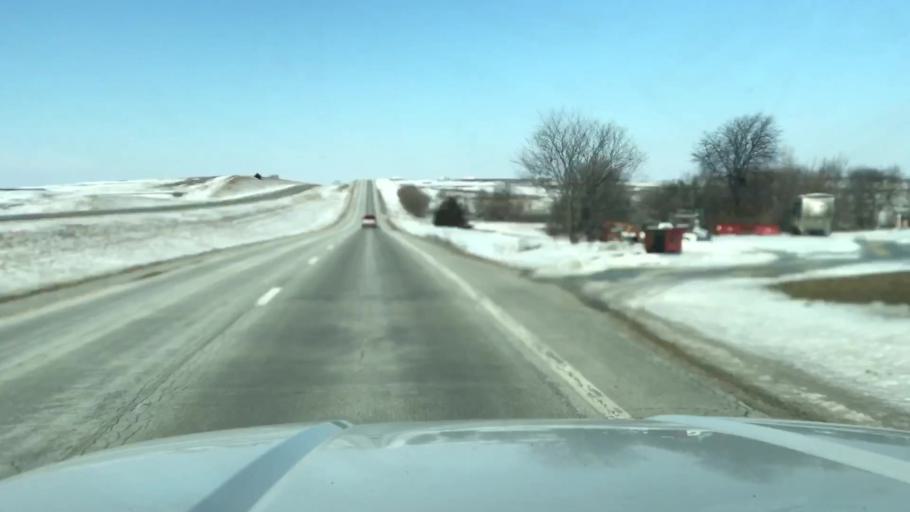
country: US
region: Missouri
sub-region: Andrew County
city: Savannah
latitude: 39.9692
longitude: -94.8696
